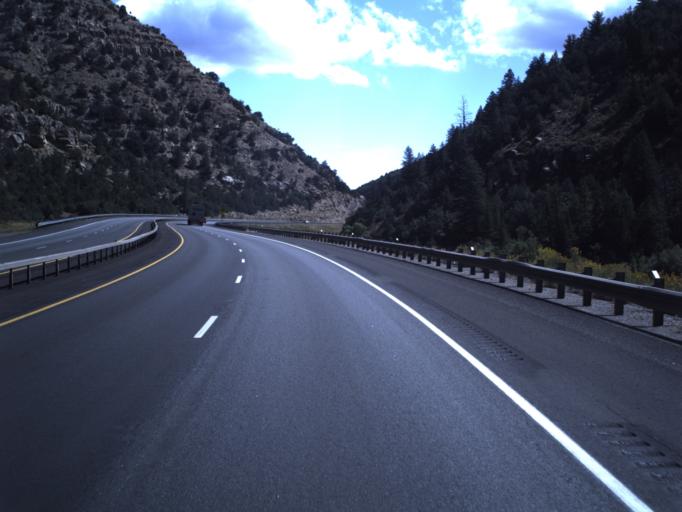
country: US
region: Utah
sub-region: Sevier County
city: Salina
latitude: 38.8845
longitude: -111.6017
